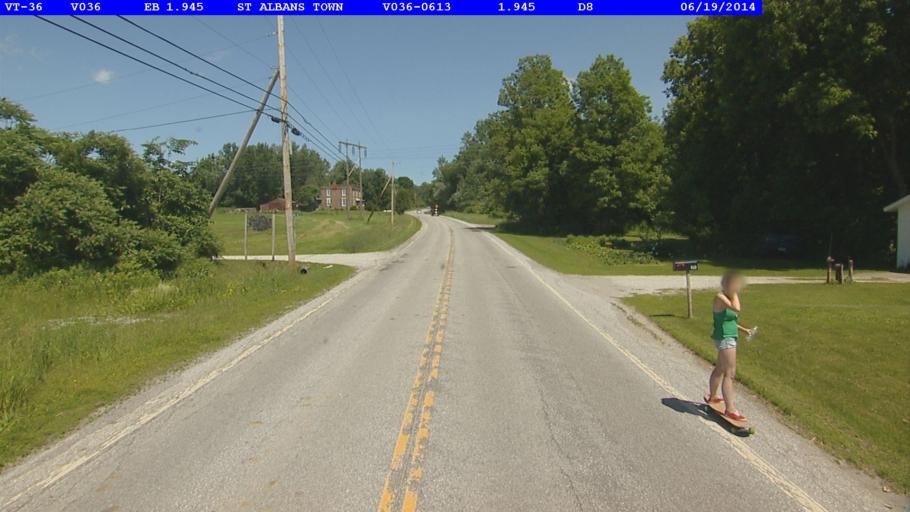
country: US
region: Vermont
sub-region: Franklin County
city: Saint Albans
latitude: 44.8115
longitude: -73.1188
